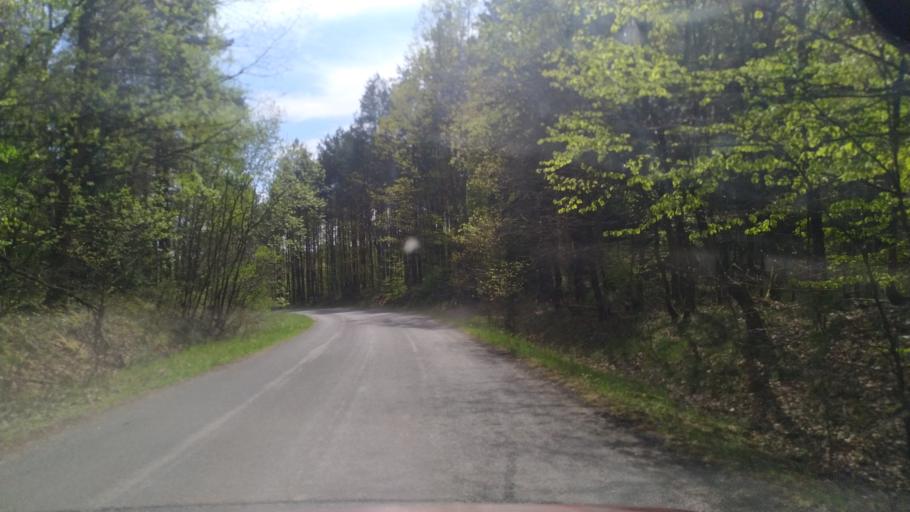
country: PL
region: West Pomeranian Voivodeship
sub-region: Powiat walecki
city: Miroslawiec
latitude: 53.3540
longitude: 16.2766
